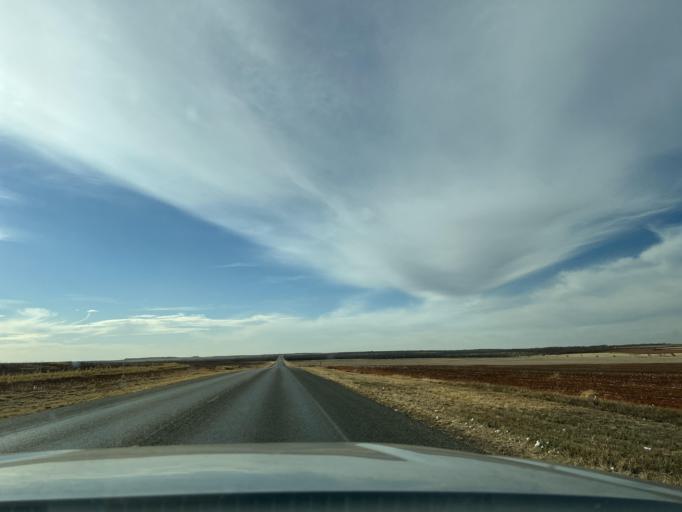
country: US
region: Texas
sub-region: Fisher County
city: Rotan
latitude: 32.7404
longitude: -100.4975
